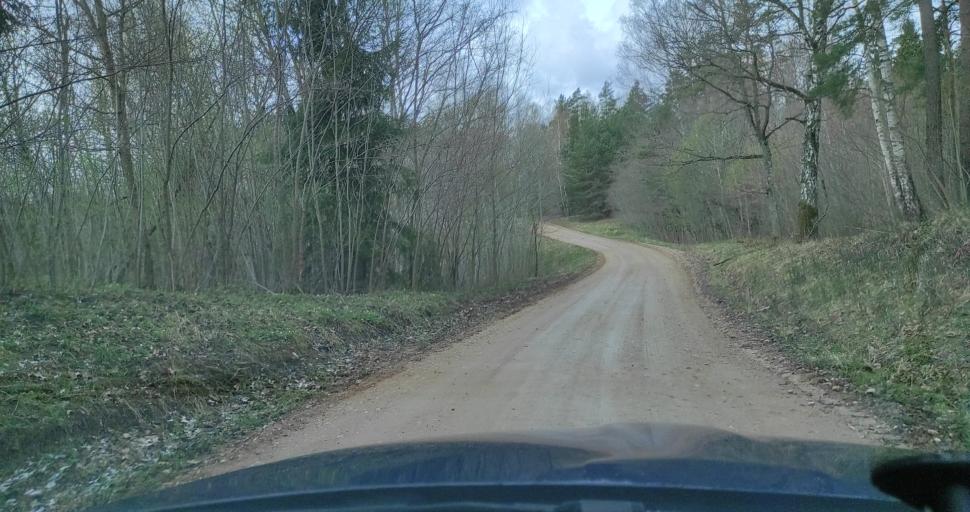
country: LV
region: Kuldigas Rajons
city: Kuldiga
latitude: 57.0571
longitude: 21.8079
